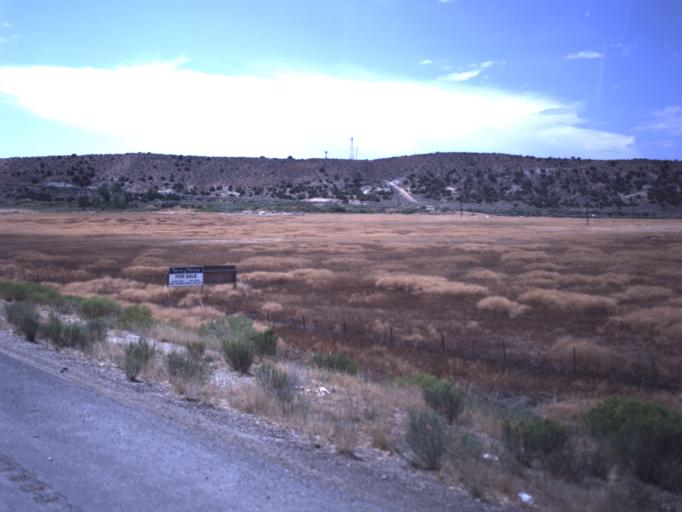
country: US
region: Utah
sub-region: Uintah County
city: Maeser
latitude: 40.4223
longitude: -109.5807
